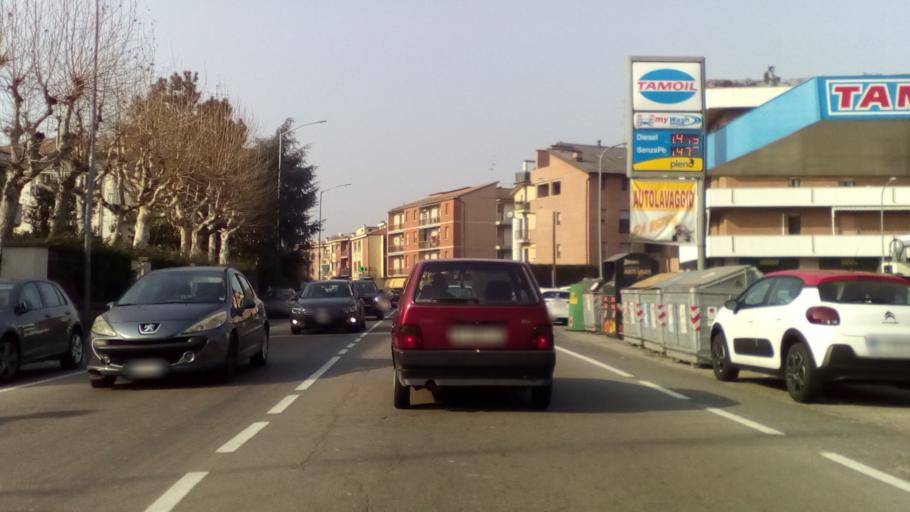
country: IT
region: Emilia-Romagna
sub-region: Provincia di Modena
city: Modena
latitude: 44.6314
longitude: 10.9408
